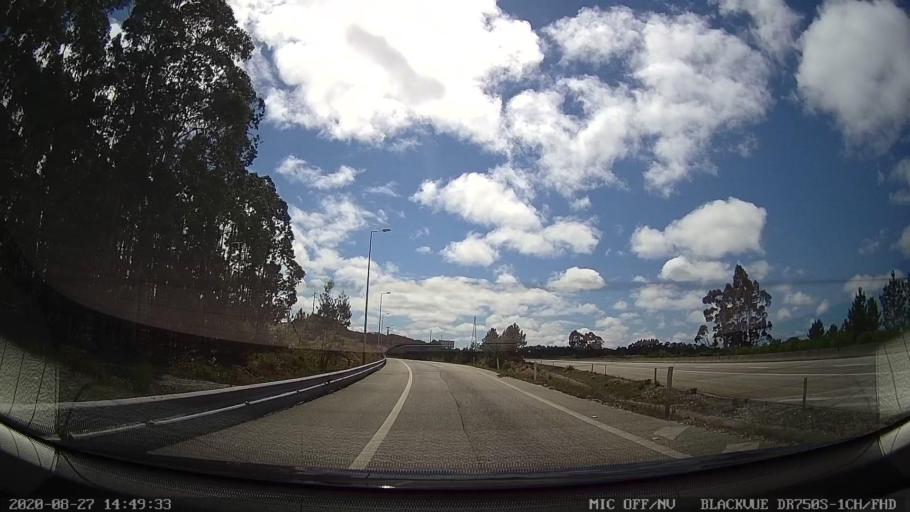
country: PT
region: Leiria
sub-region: Marinha Grande
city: Marinha Grande
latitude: 39.7404
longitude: -8.8807
